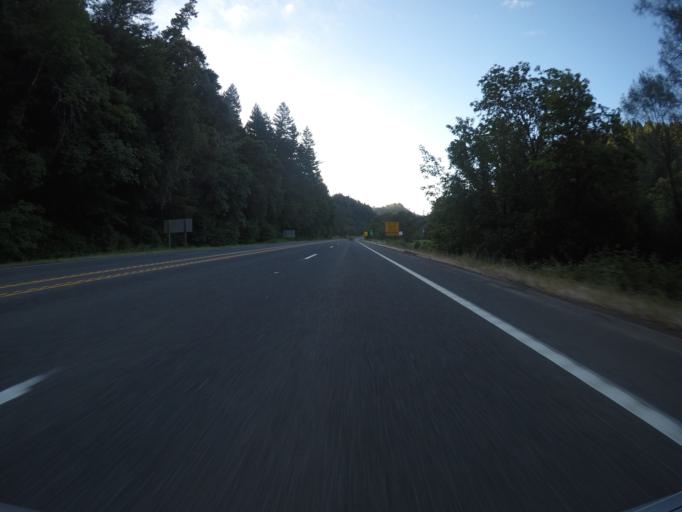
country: US
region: California
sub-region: Mendocino County
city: Brooktrails
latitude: 39.5532
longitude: -123.4274
